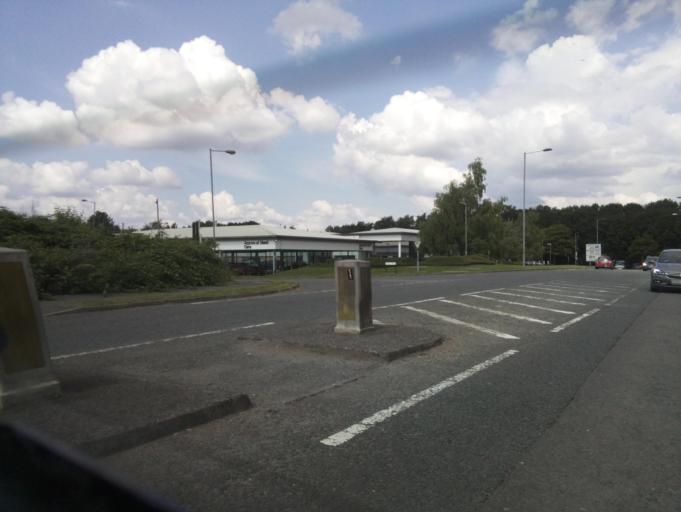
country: GB
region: England
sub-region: Borough of Swindon
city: Swindon
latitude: 51.5535
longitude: -1.8068
